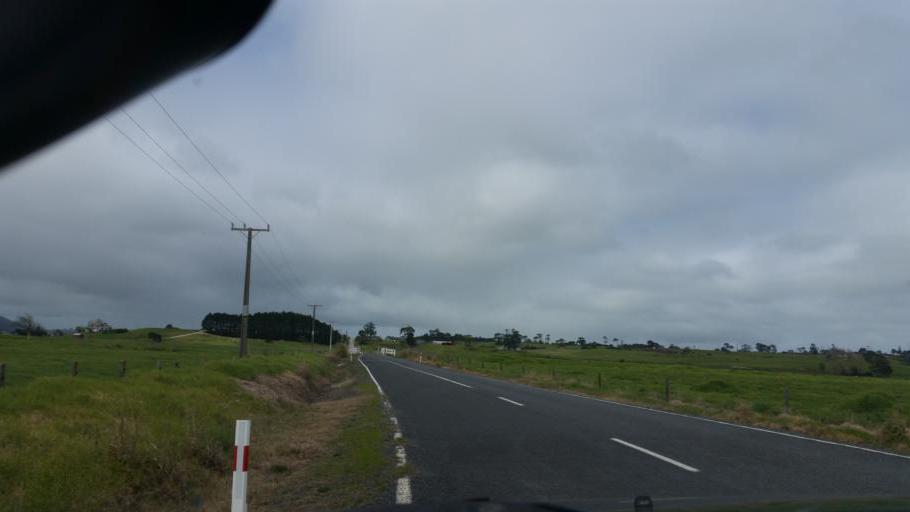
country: NZ
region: Northland
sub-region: Kaipara District
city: Dargaville
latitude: -36.0073
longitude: 173.8869
